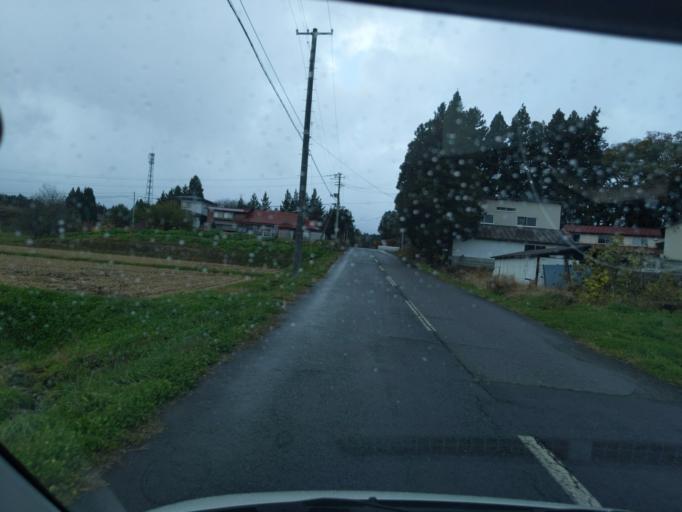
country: JP
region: Iwate
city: Mizusawa
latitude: 39.0943
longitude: 140.9892
